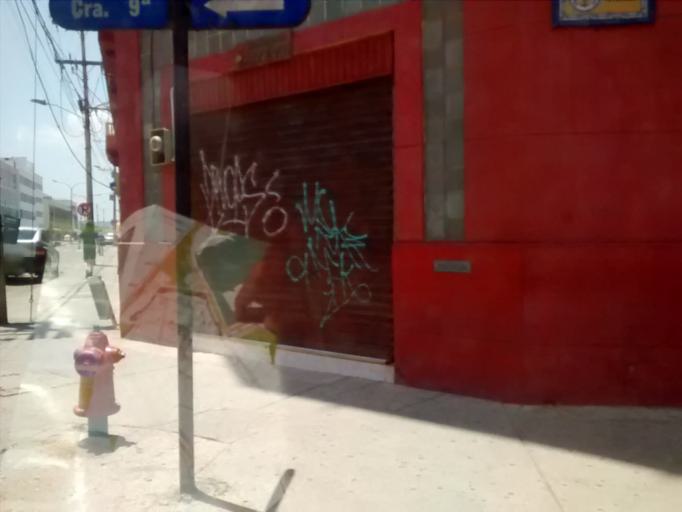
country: CO
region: Bolivar
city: Cartagena
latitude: 10.4236
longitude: -75.5463
